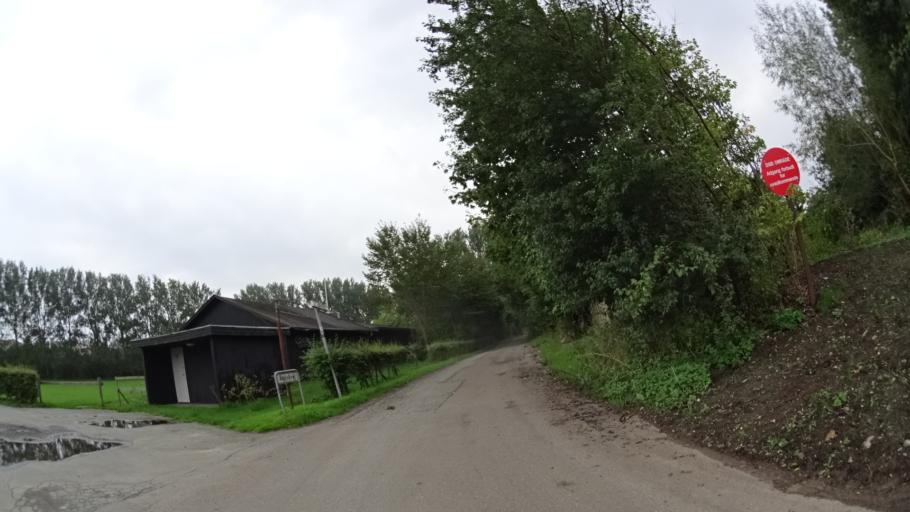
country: DK
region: Central Jutland
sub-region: Arhus Kommune
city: Arhus
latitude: 56.1495
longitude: 10.1795
